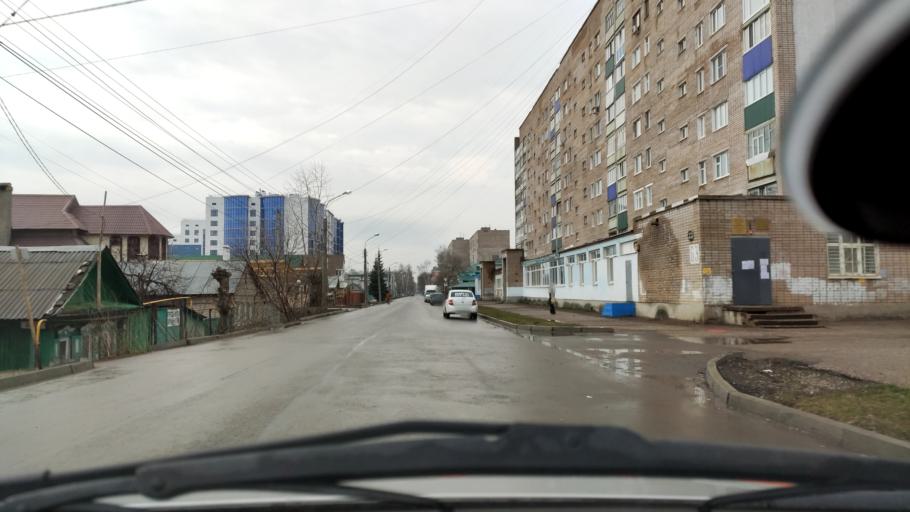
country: RU
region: Bashkortostan
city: Sterlitamak
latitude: 53.6236
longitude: 55.9571
